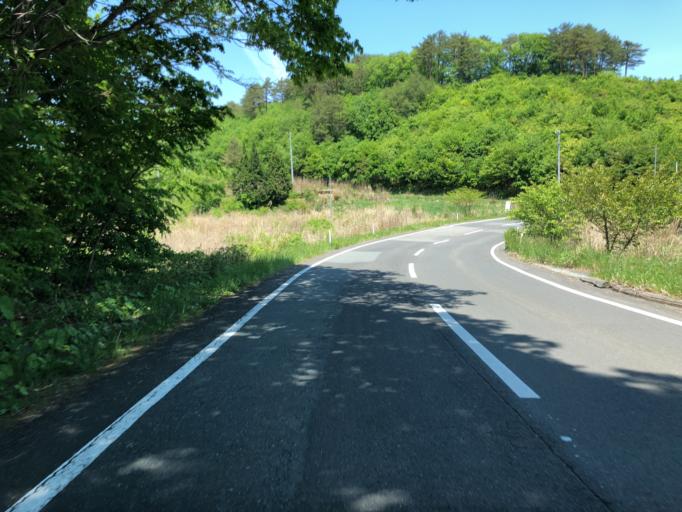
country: JP
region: Fukushima
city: Namie
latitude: 37.5253
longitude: 140.8017
